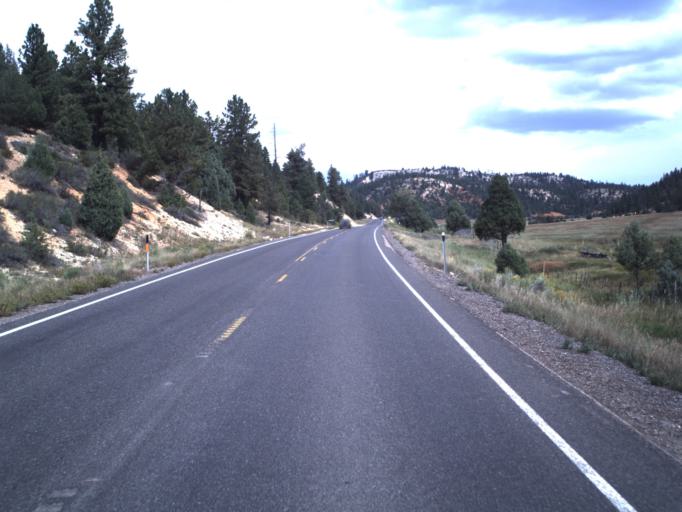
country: US
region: Utah
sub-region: Kane County
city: Kanab
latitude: 37.4327
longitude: -112.5386
